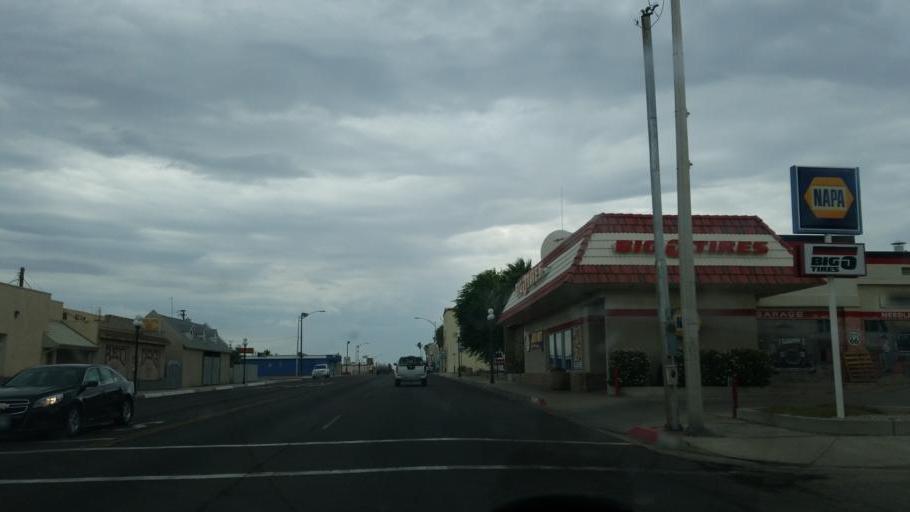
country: US
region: California
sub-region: San Bernardino County
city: Needles
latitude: 34.8398
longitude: -114.6070
